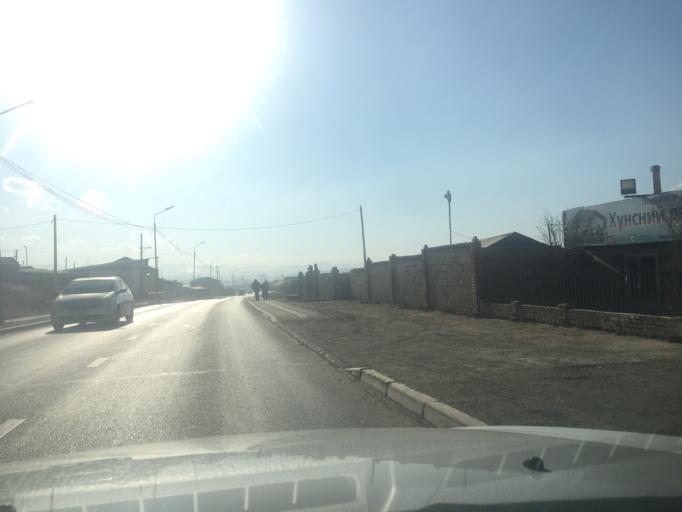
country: MN
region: Ulaanbaatar
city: Ulaanbaatar
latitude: 47.9627
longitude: 106.8283
